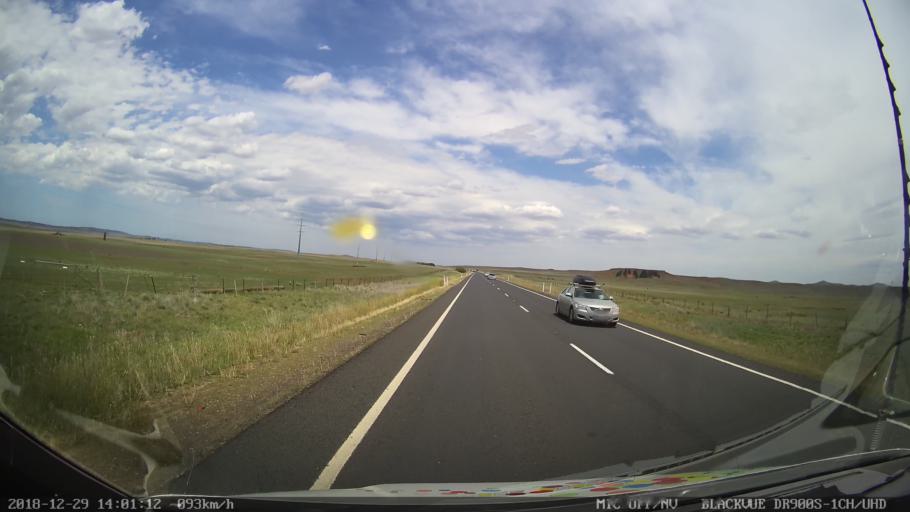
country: AU
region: New South Wales
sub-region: Cooma-Monaro
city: Cooma
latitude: -36.2723
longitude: 149.1666
